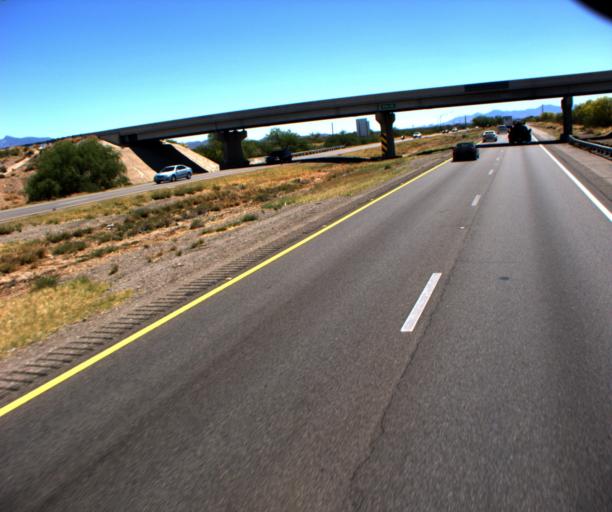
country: US
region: Arizona
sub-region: Pima County
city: Vail
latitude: 32.0821
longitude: -110.8066
